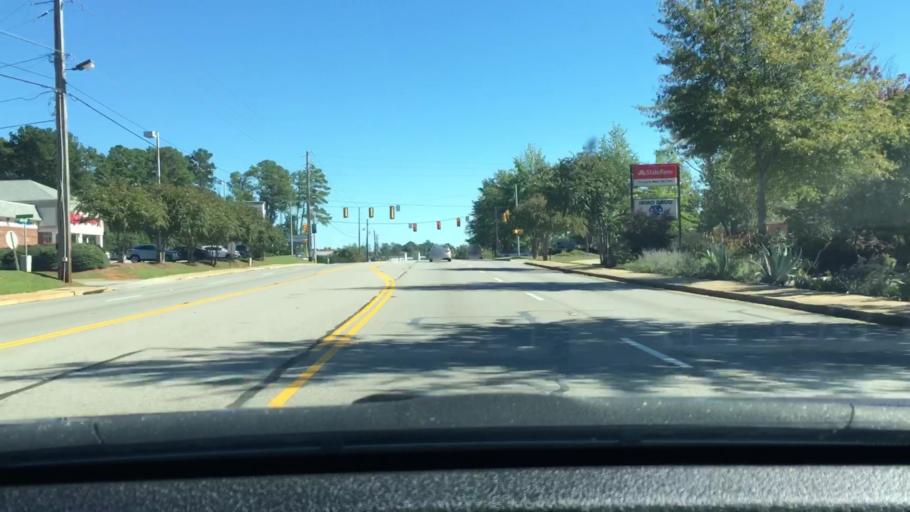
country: US
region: South Carolina
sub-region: Lexington County
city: Irmo
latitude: 34.0892
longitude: -81.1752
